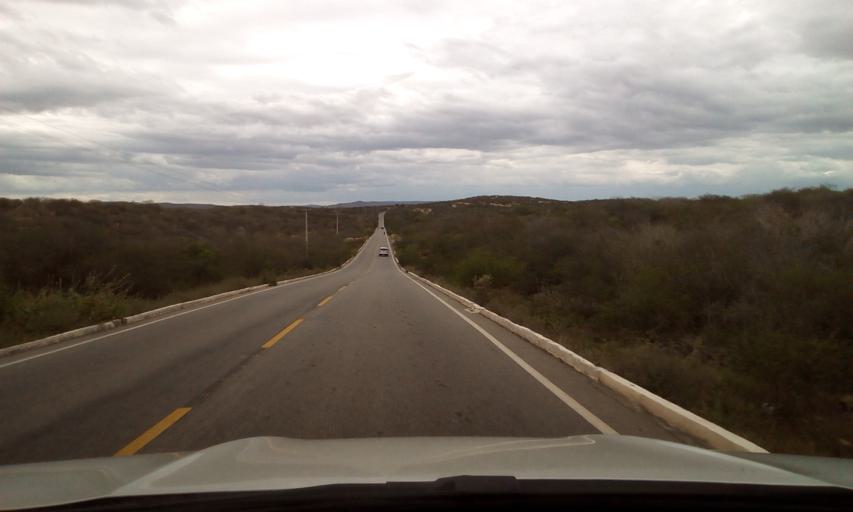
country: BR
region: Paraiba
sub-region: Picui
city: Picui
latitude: -6.5265
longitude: -36.3191
